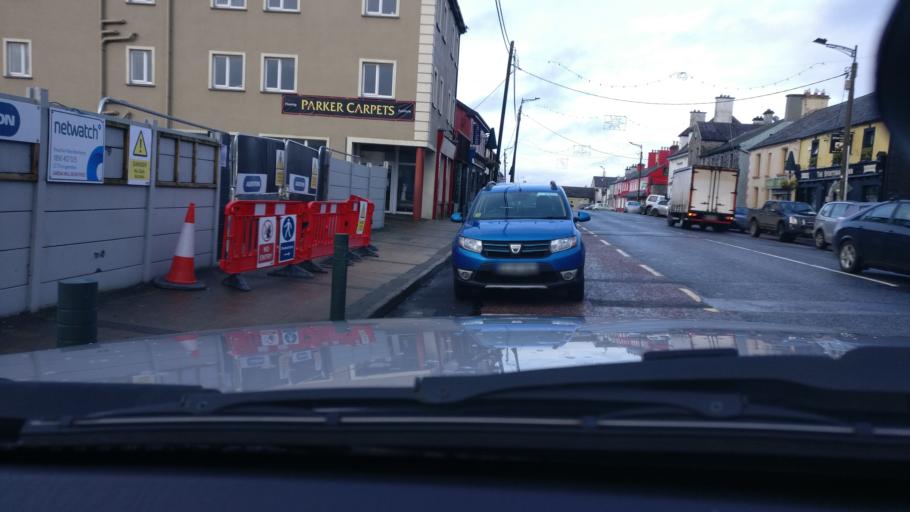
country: IE
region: Leinster
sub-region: An Longfort
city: Edgeworthstown
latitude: 53.6956
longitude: -7.6084
